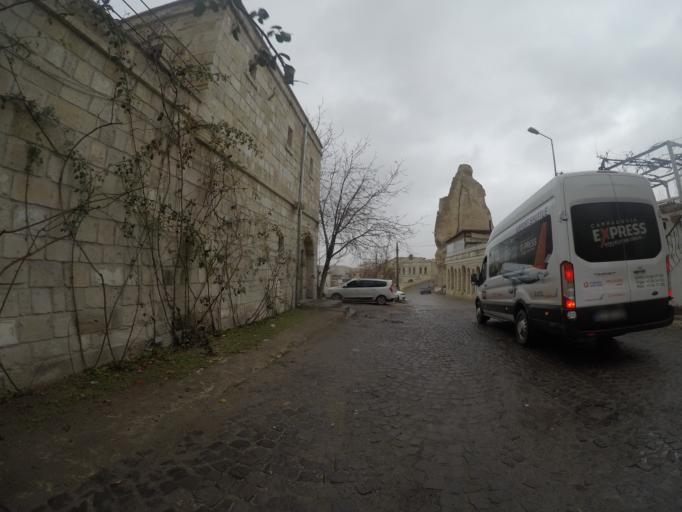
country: TR
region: Nevsehir
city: Goereme
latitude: 38.6426
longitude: 34.8320
